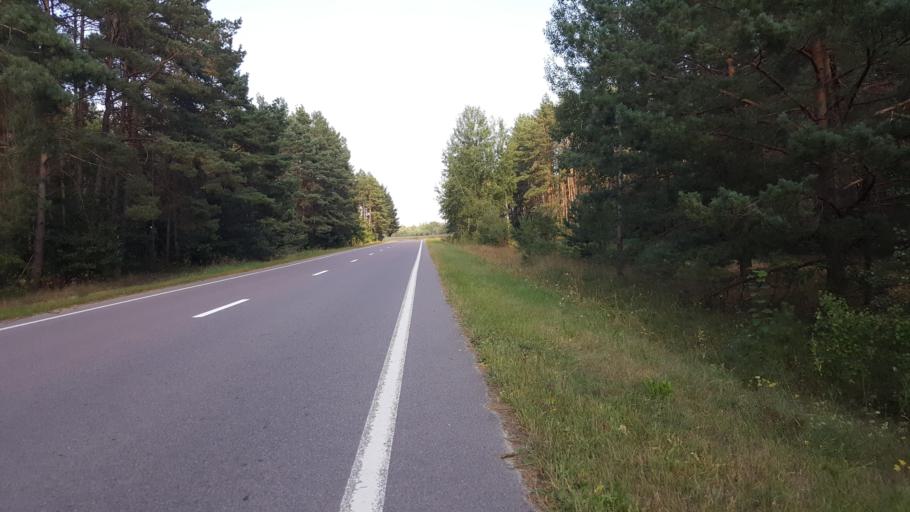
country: PL
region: Podlasie
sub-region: Powiat hajnowski
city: Hajnowka
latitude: 52.5556
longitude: 23.5964
